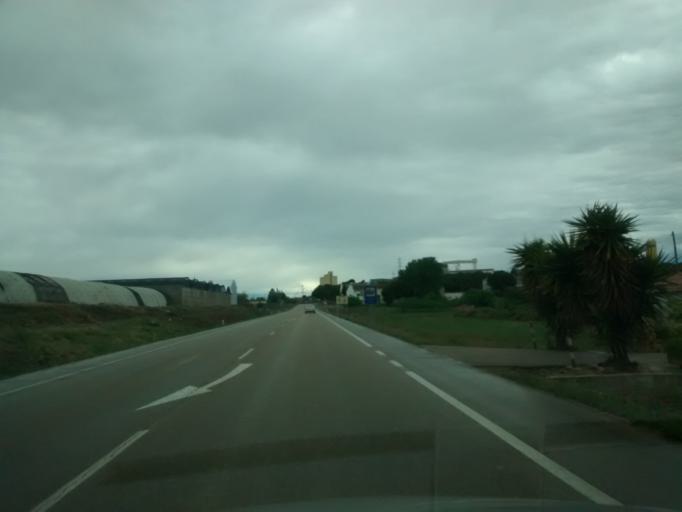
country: ES
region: Aragon
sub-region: Provincia de Zaragoza
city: Caspe
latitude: 41.2234
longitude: -0.0235
